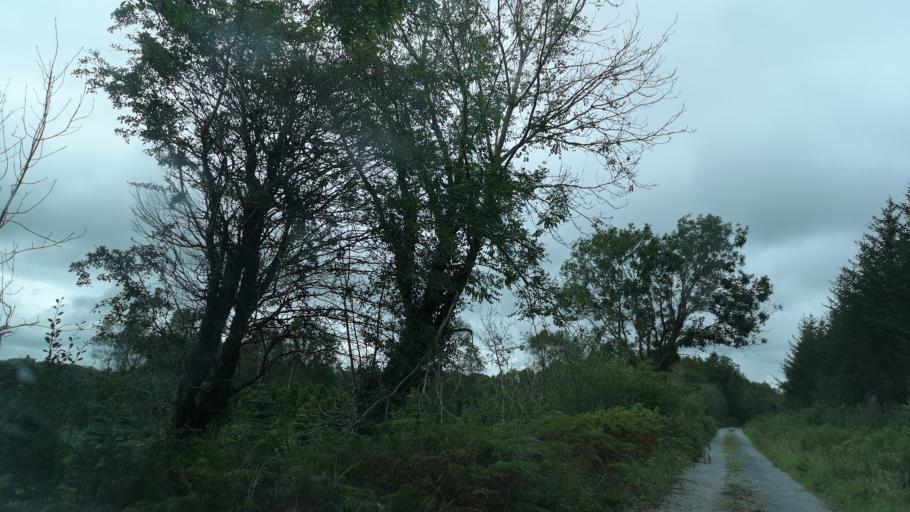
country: IE
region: Connaught
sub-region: County Galway
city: Athenry
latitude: 53.3005
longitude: -8.6674
